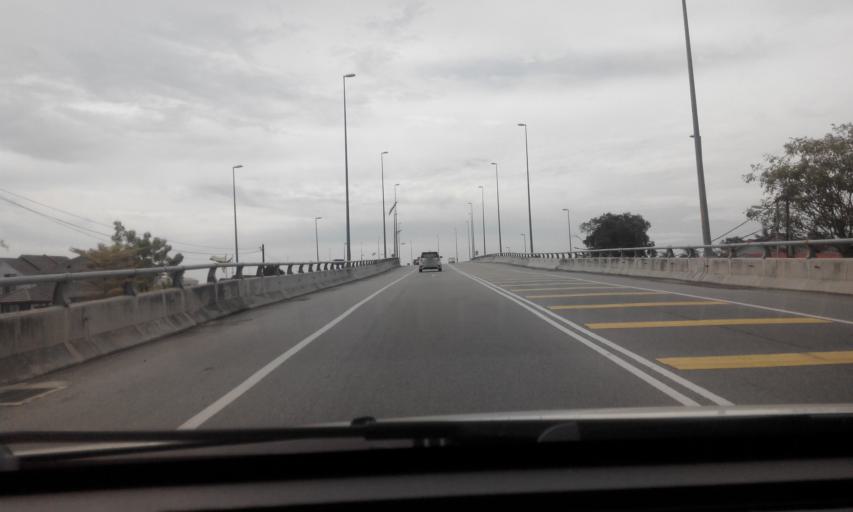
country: MY
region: Perak
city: Parit Buntar
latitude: 5.1310
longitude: 100.4884
